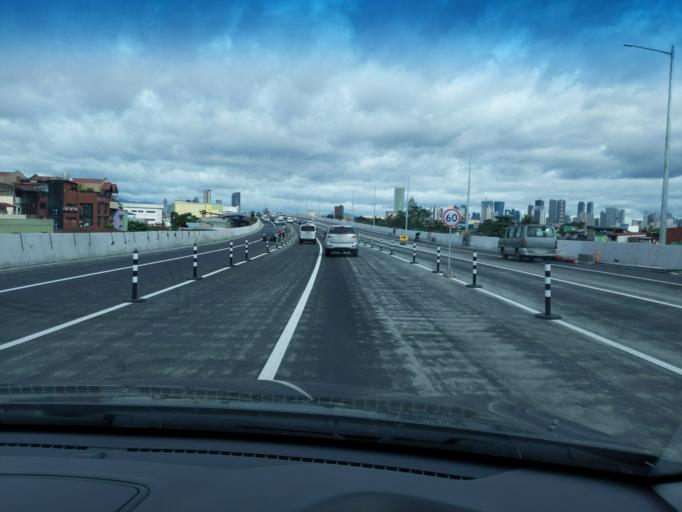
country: PH
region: Metro Manila
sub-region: San Juan
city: San Juan
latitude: 14.5888
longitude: 121.0185
